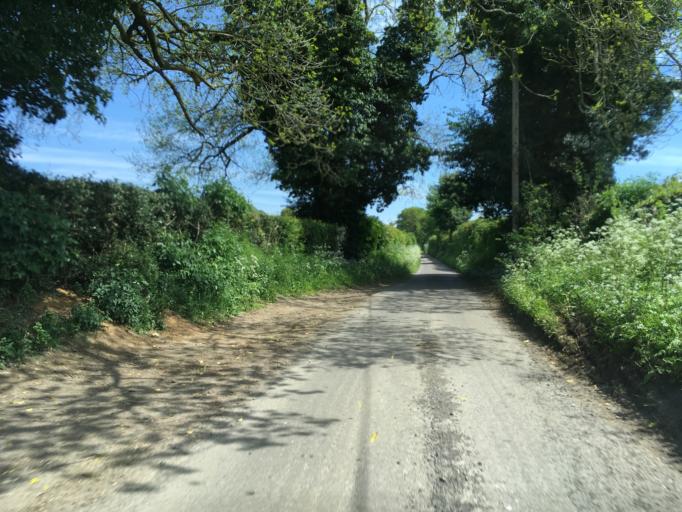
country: GB
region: England
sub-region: Gloucestershire
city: Dursley
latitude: 51.6629
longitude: -2.3582
